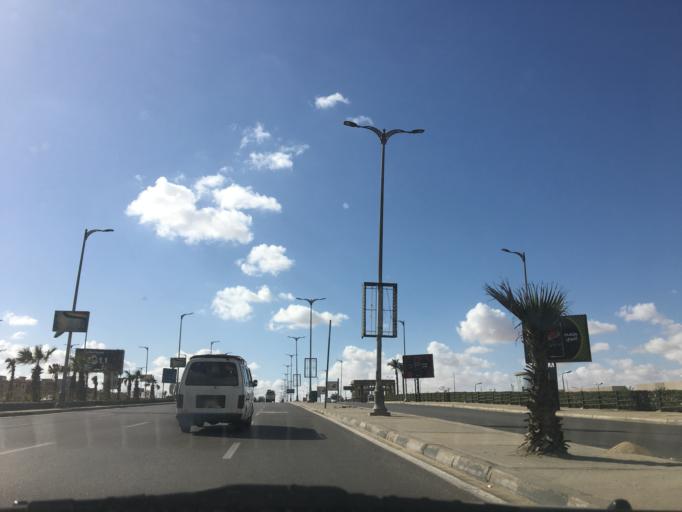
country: EG
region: Al Jizah
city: Awsim
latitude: 30.0073
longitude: 30.9787
